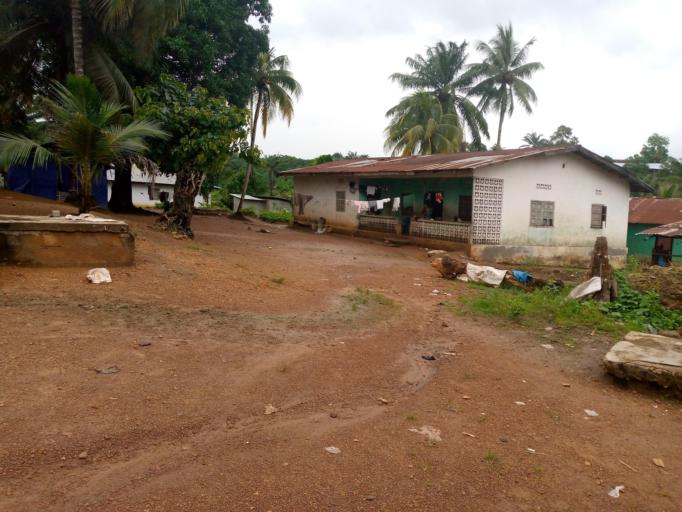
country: SL
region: Eastern Province
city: Kenema
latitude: 7.8811
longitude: -11.1769
